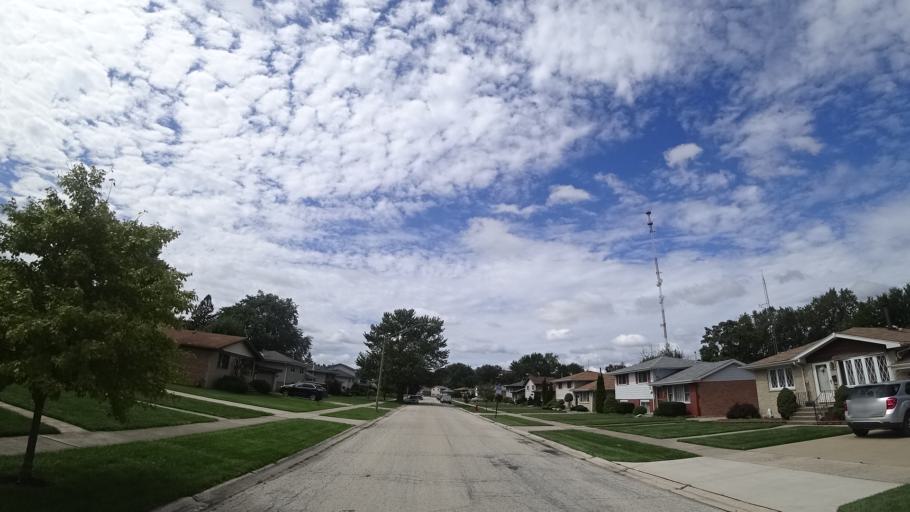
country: US
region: Illinois
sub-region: Cook County
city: Chicago Ridge
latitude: 41.7067
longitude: -87.7809
